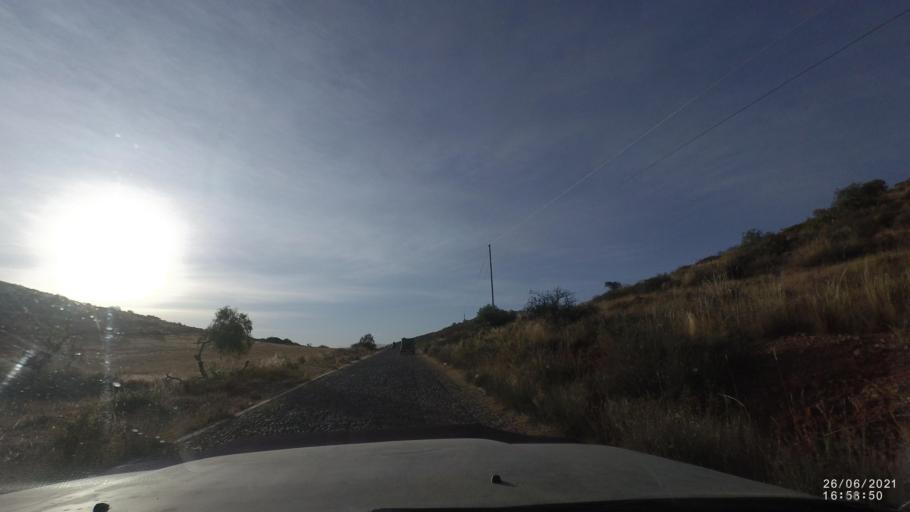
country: BO
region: Cochabamba
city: Cliza
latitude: -17.6696
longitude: -65.9055
